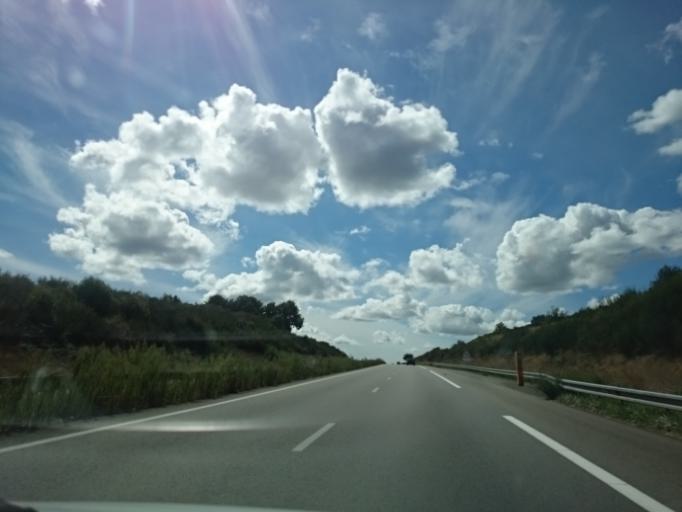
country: FR
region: Pays de la Loire
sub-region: Departement de la Loire-Atlantique
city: Couffe
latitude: 47.3687
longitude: -1.2987
